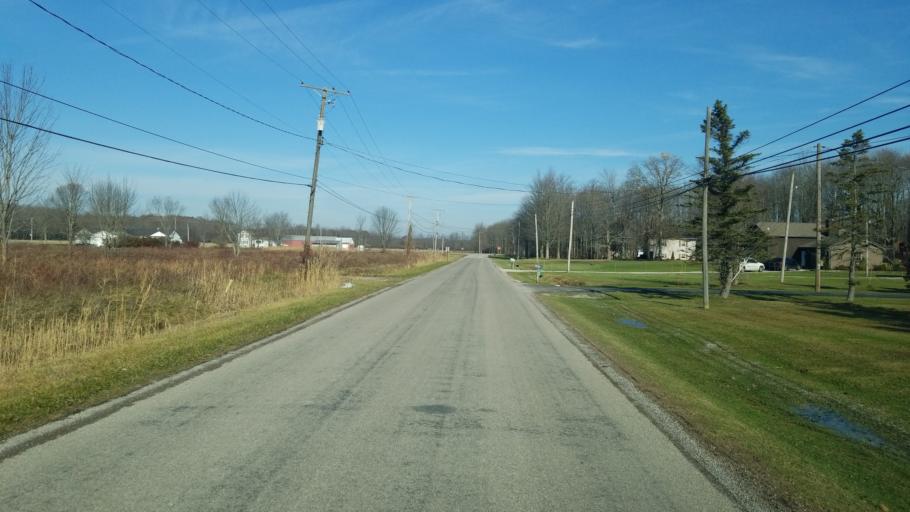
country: US
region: Ohio
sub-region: Ashtabula County
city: Jefferson
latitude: 41.7440
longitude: -80.7488
